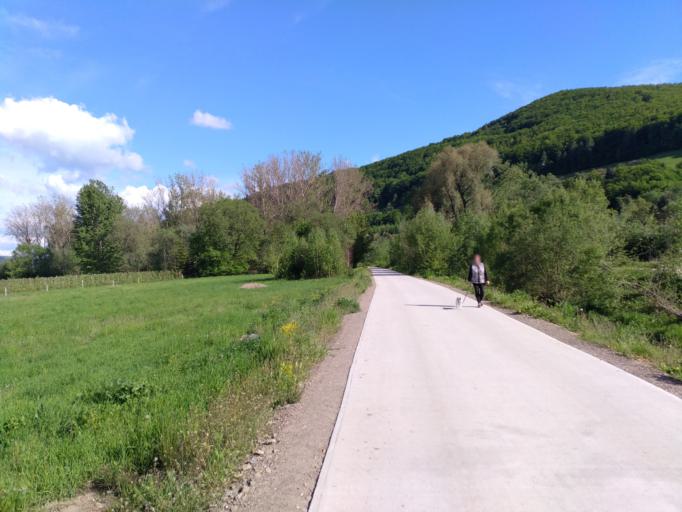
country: PL
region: Lesser Poland Voivodeship
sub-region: Powiat nowosadecki
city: Lacko
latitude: 49.5514
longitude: 20.4384
